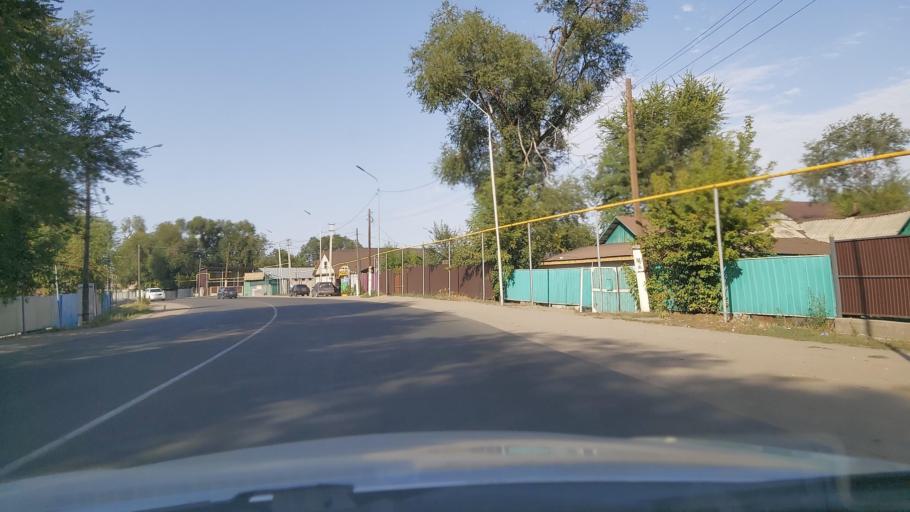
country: KZ
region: Almaty Oblysy
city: Energeticheskiy
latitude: 43.4954
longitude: 77.0397
